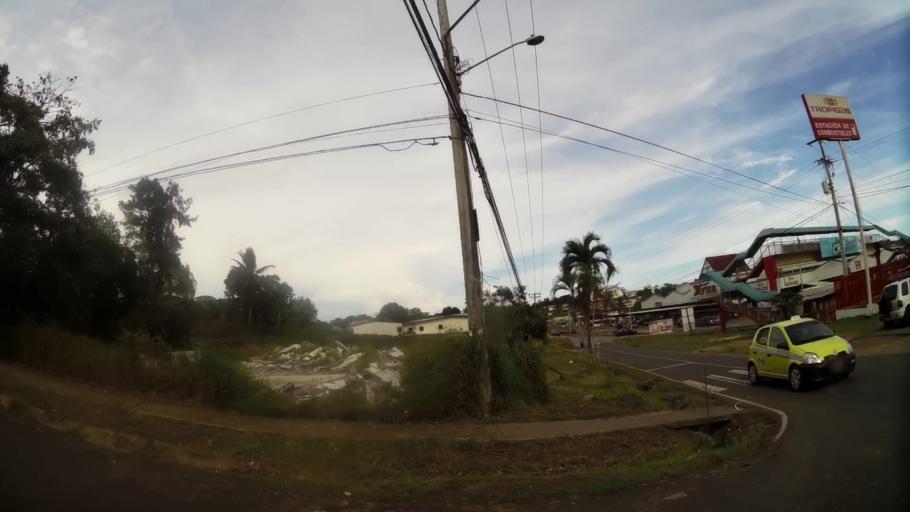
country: PA
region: Panama
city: El Coco
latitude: 8.8705
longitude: -79.8019
